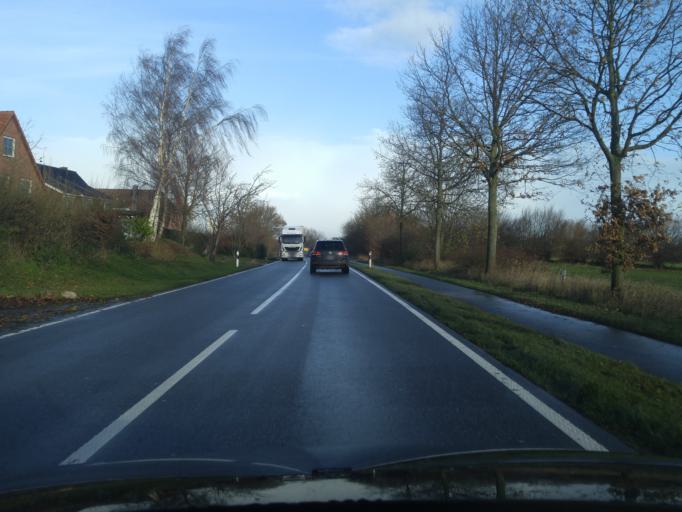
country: DE
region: Schleswig-Holstein
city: Timmendorfer Strand
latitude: 53.9838
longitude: 10.7731
